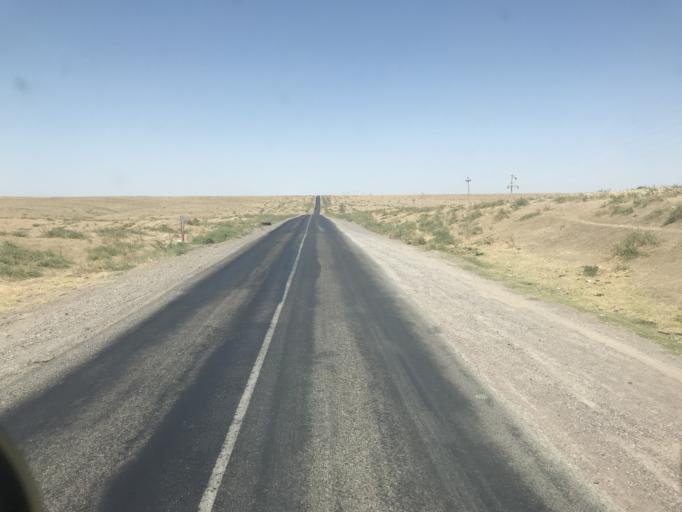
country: UZ
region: Toshkent
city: Chinoz
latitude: 41.1375
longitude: 68.7104
